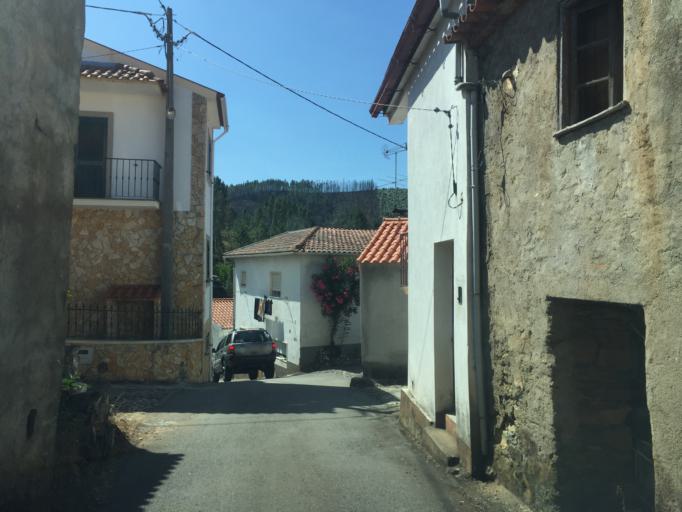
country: PT
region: Coimbra
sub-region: Pampilhosa da Serra
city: Pampilhosa da Serra
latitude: 40.0298
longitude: -7.8255
